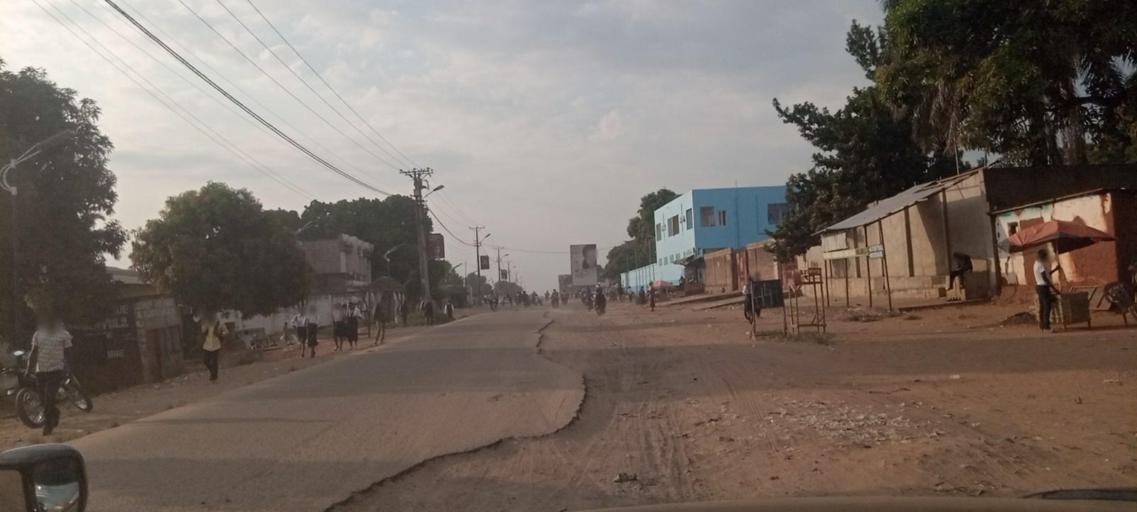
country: CD
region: Kasai-Oriental
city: Mbuji-Mayi
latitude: -6.1301
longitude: 23.6047
